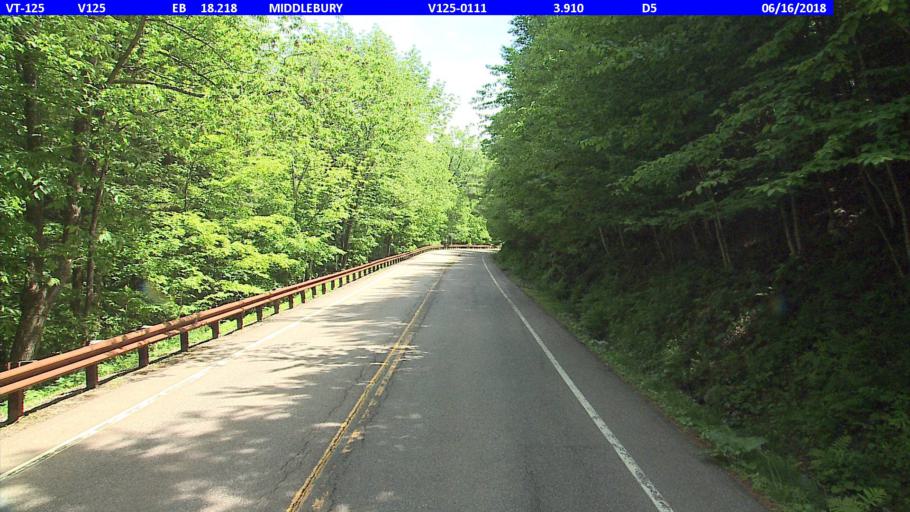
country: US
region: Vermont
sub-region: Addison County
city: Middlebury (village)
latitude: 43.9740
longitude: -73.0662
